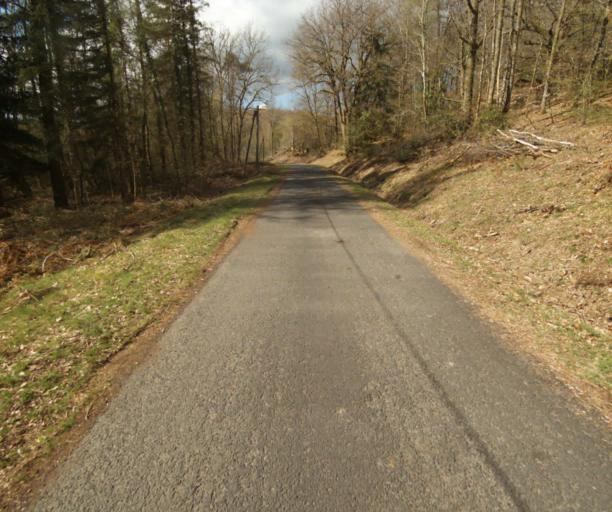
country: FR
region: Limousin
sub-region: Departement de la Correze
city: Argentat
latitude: 45.2364
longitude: 1.9519
